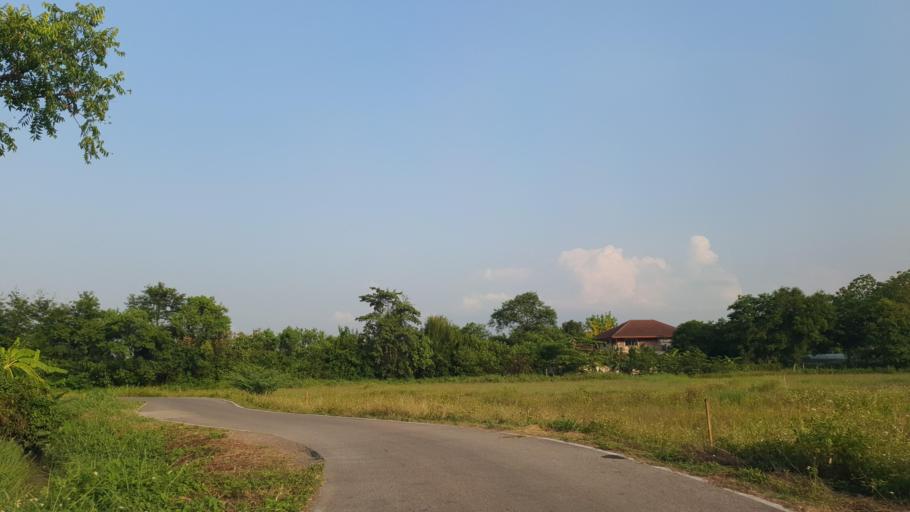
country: TH
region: Chiang Mai
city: San Pa Tong
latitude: 18.6389
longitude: 98.8751
